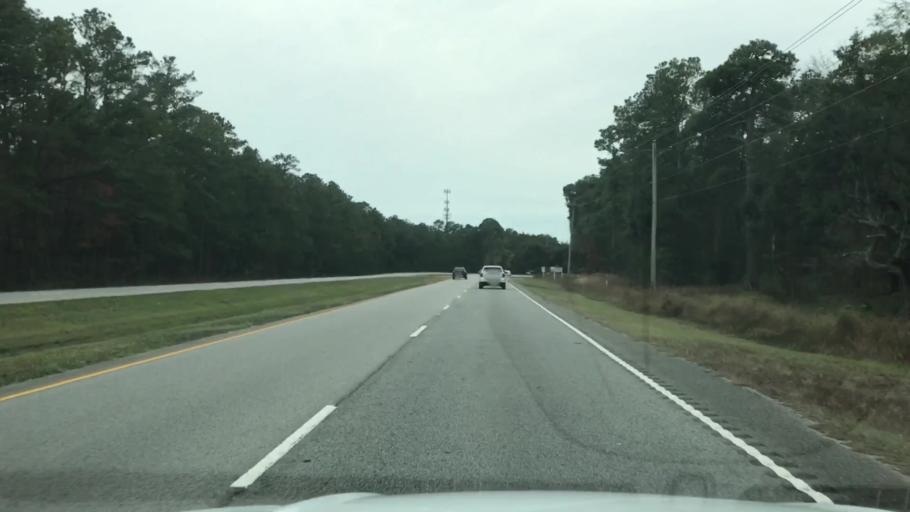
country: US
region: South Carolina
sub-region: Georgetown County
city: Georgetown
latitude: 33.3687
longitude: -79.2201
